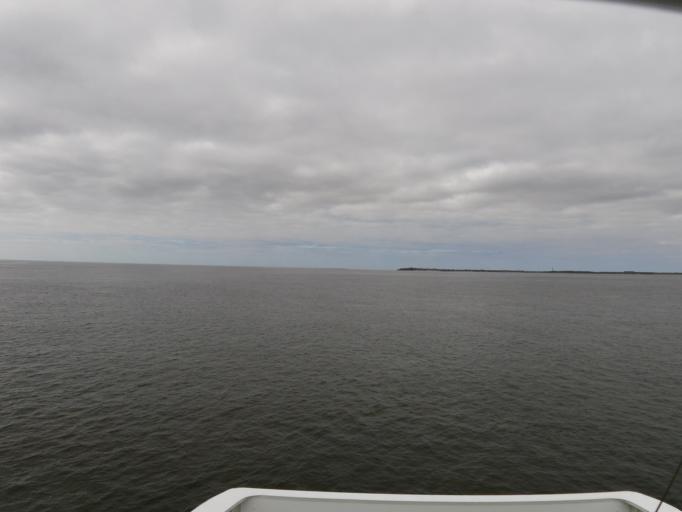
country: DE
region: Schleswig-Holstein
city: Witsum
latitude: 54.6428
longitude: 8.4524
